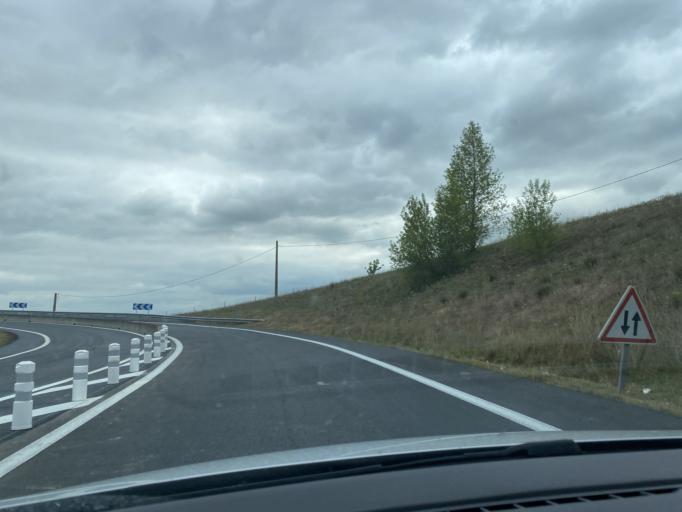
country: FR
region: Midi-Pyrenees
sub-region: Departement de la Haute-Garonne
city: Nailloux
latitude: 43.3869
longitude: 1.6225
